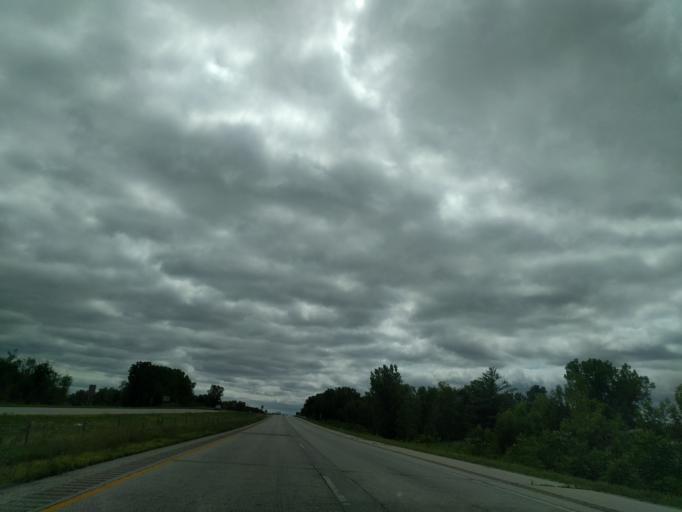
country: US
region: Wisconsin
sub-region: Brown County
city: Suamico
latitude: 44.6440
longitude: -88.0490
